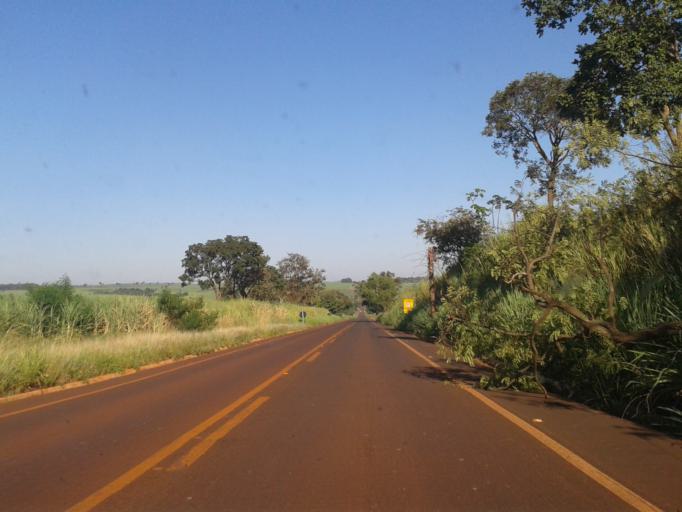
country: BR
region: Minas Gerais
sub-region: Capinopolis
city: Capinopolis
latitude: -18.7010
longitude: -49.6585
